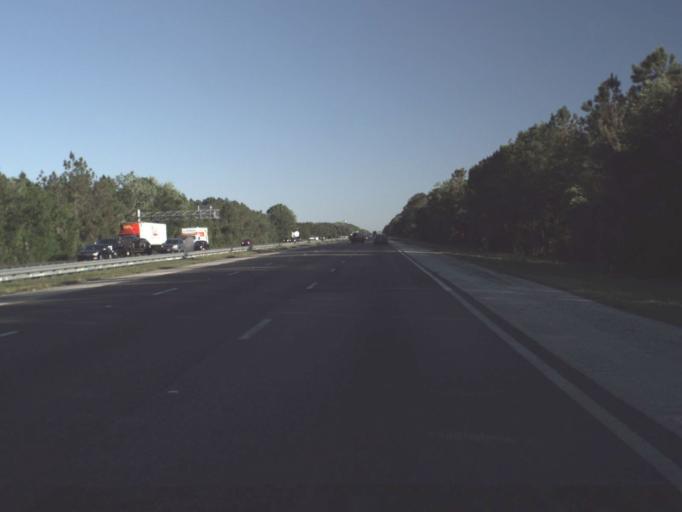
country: US
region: Florida
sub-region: Flagler County
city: Palm Coast
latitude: 29.5849
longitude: -81.2392
